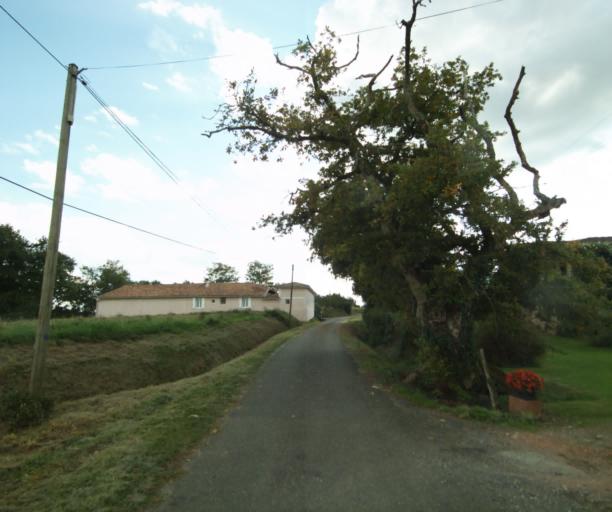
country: FR
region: Midi-Pyrenees
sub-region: Departement du Gers
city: Cazaubon
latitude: 43.8876
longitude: -0.0514
